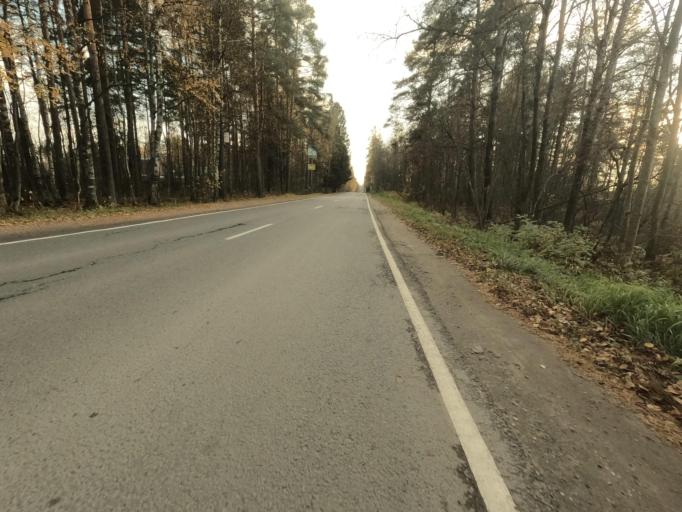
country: RU
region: St.-Petersburg
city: Beloostrov
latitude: 60.1659
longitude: 30.0098
